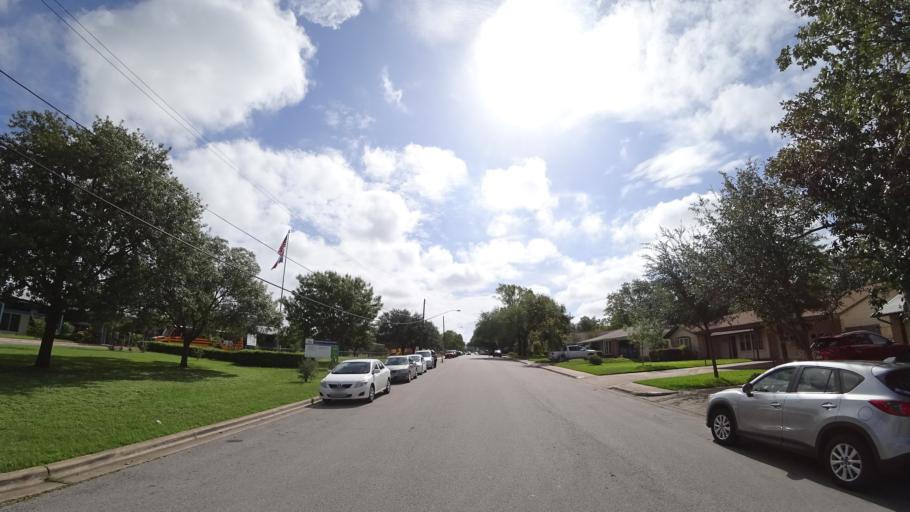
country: US
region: Texas
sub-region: Travis County
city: West Lake Hills
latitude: 30.3523
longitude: -97.7379
